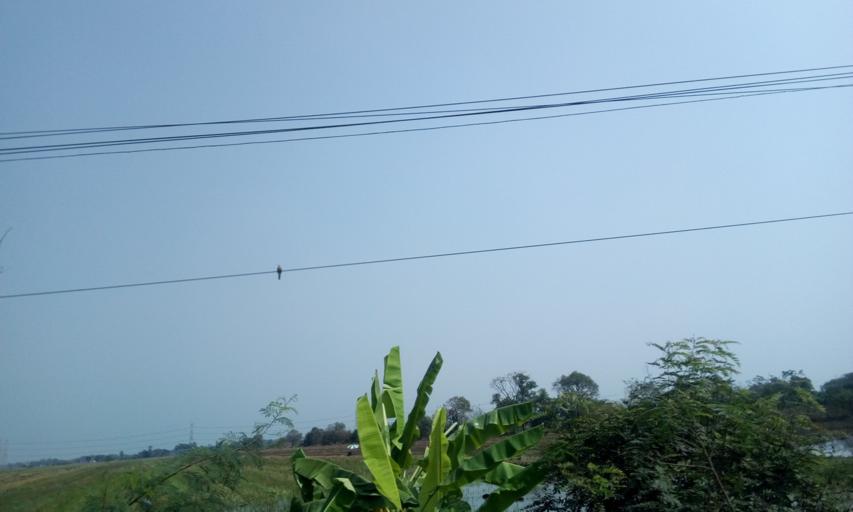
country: TH
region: Pathum Thani
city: Ban Rangsit
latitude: 14.0073
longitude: 100.7571
